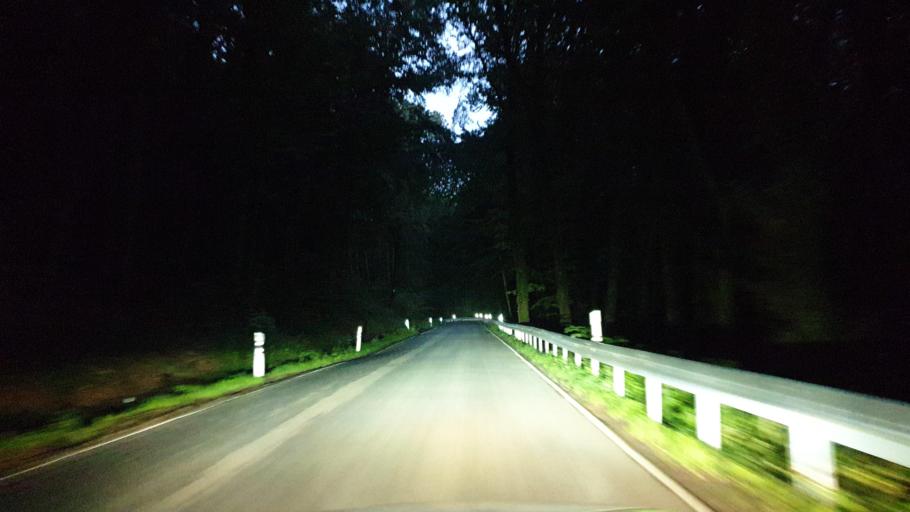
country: DE
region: North Rhine-Westphalia
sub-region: Regierungsbezirk Detmold
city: Huellhorst
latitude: 52.2874
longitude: 8.7104
